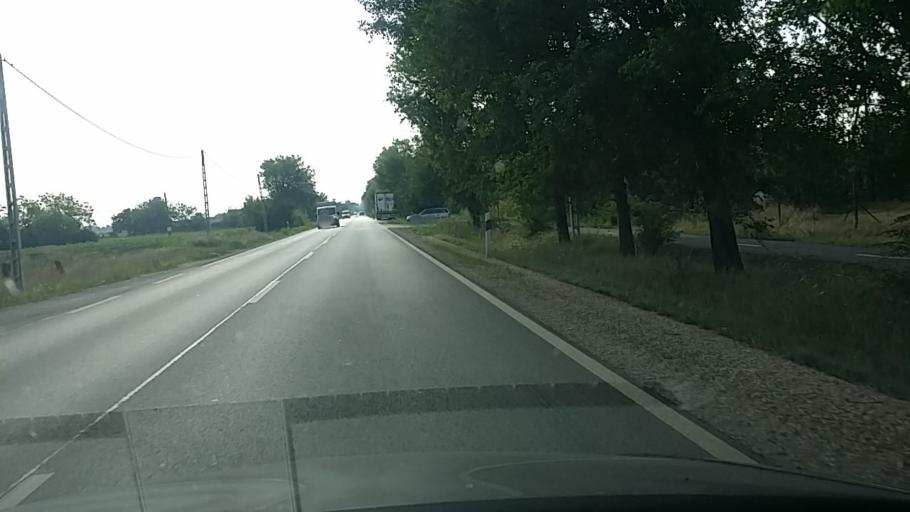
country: HU
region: Bekes
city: Szarvas
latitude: 46.8486
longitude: 20.5950
